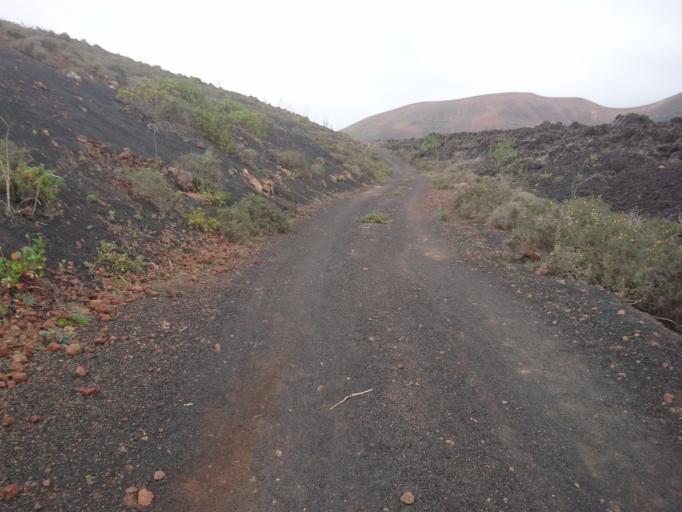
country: ES
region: Canary Islands
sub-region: Provincia de Las Palmas
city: Tinajo
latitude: 29.0153
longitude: -13.6927
